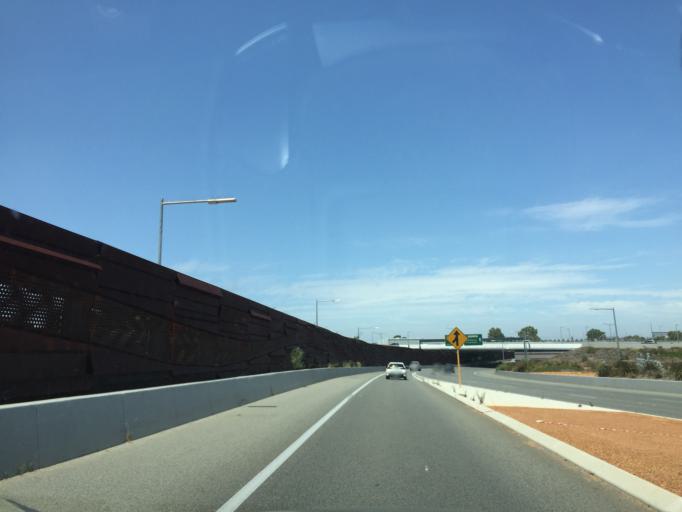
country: AU
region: Western Australia
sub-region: Belmont
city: Kewdale
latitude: -31.9653
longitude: 115.9564
